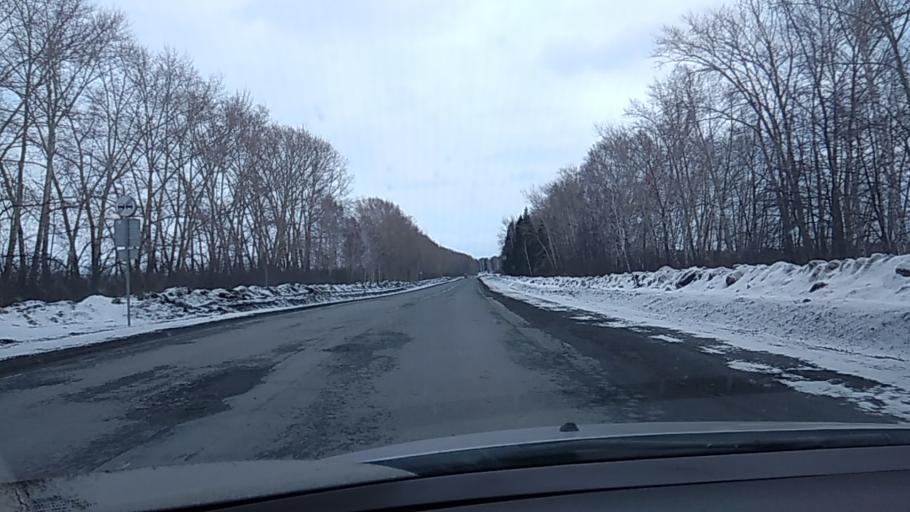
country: RU
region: Sverdlovsk
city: Dvurechensk
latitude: 56.6479
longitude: 61.2066
